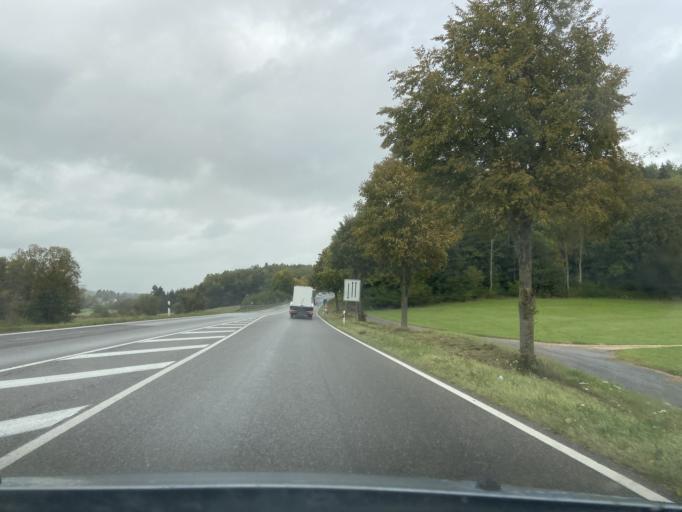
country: DE
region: Baden-Wuerttemberg
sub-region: Tuebingen Region
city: Messkirch
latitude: 47.9974
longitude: 9.1301
